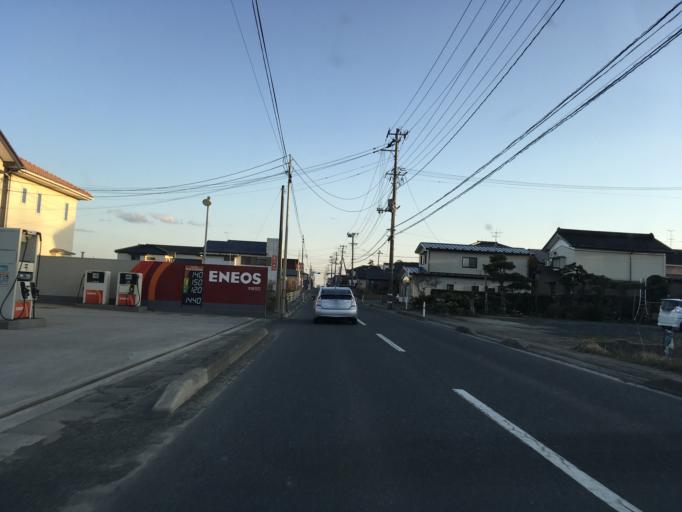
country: JP
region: Iwate
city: Ofunato
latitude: 38.8207
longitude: 141.5730
